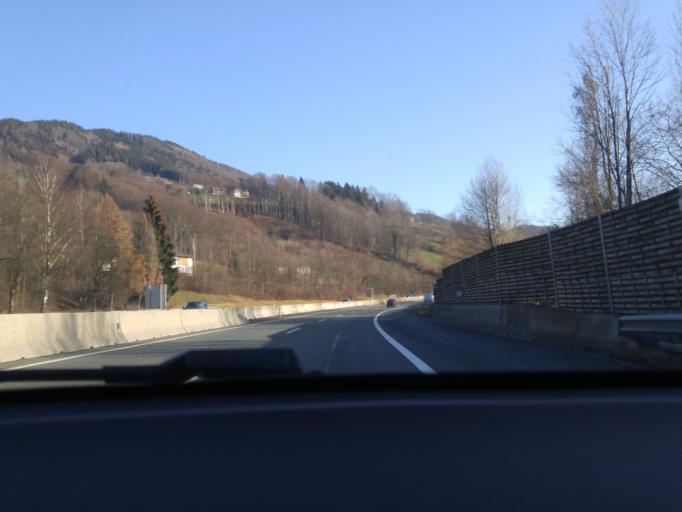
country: AT
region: Upper Austria
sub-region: Politischer Bezirk Vocklabruck
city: Mondsee
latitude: 47.8634
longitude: 13.3443
